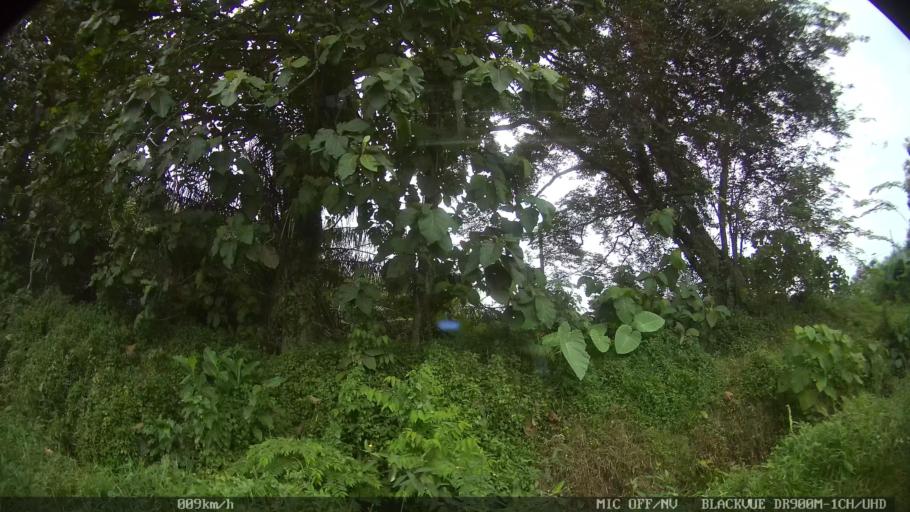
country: ID
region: North Sumatra
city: Sunggal
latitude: 3.6198
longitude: 98.5806
